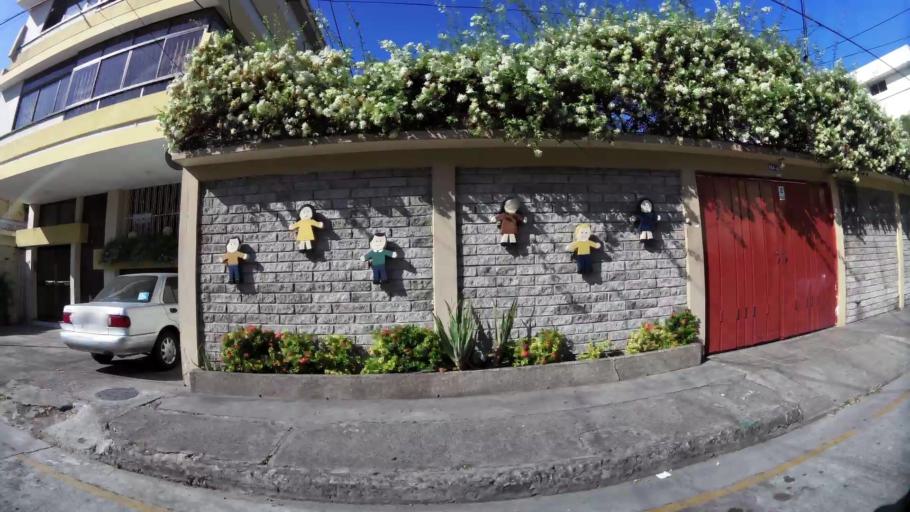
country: EC
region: Guayas
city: Guayaquil
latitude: -2.1761
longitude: -79.8969
